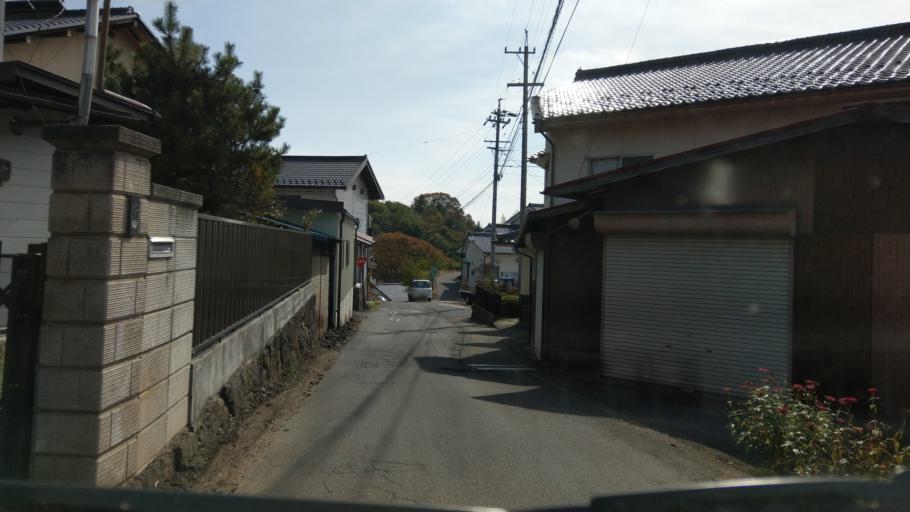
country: JP
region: Nagano
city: Komoro
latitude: 36.3512
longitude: 138.4313
